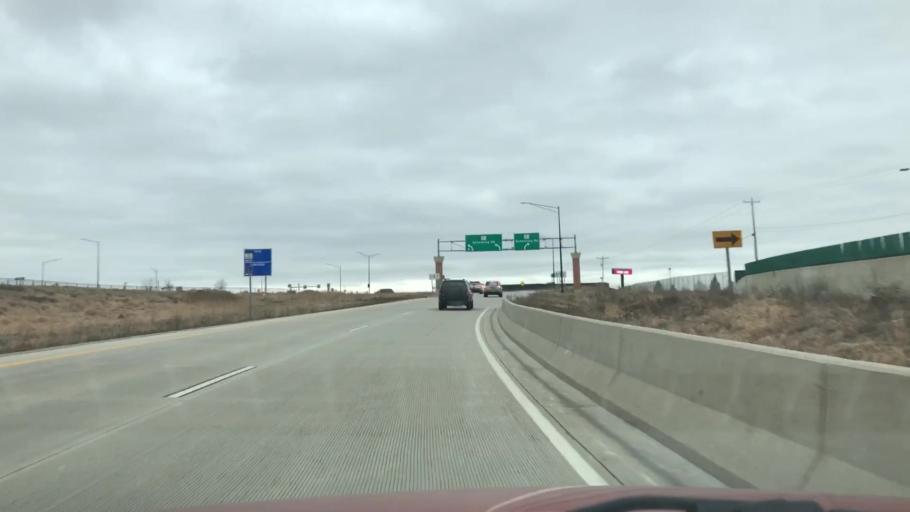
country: US
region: Wisconsin
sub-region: Brown County
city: De Pere
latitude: 44.4315
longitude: -88.1120
